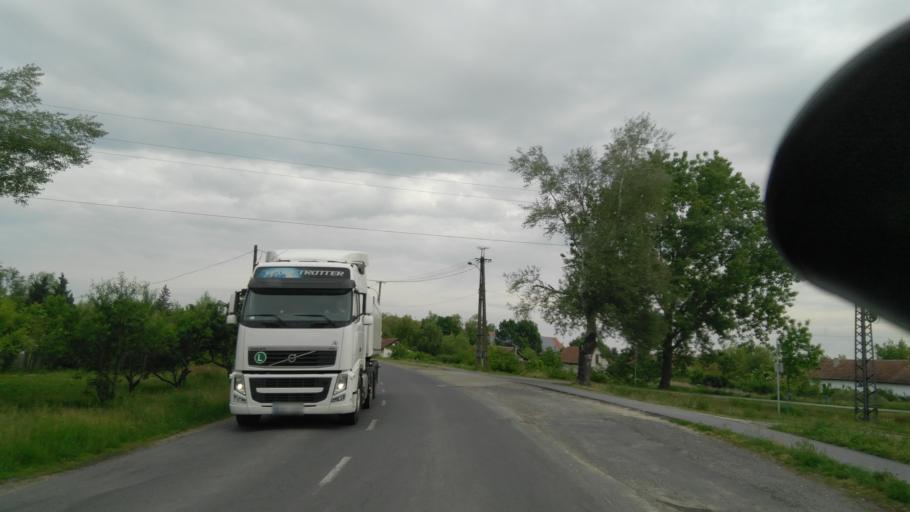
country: HU
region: Bekes
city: Veszto
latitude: 46.9085
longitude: 21.2582
